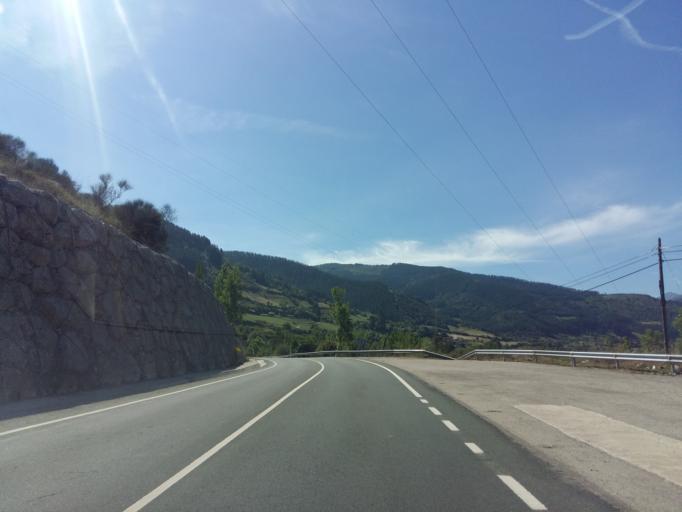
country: ES
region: Cantabria
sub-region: Provincia de Cantabria
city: Potes
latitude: 43.1868
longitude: -4.6046
